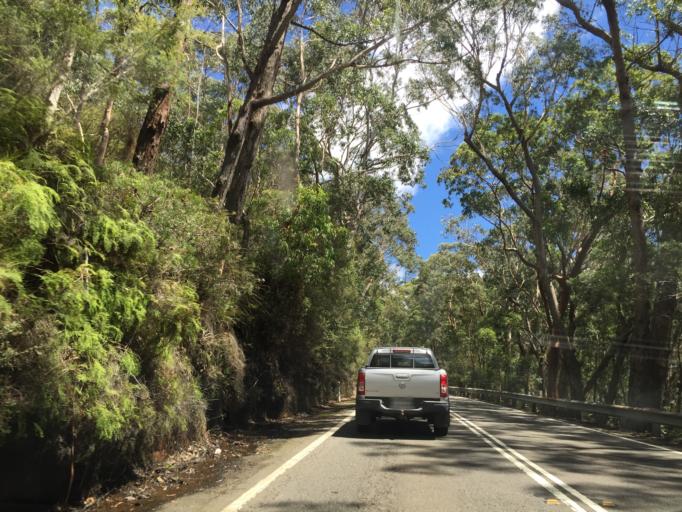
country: AU
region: New South Wales
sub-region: Blue Mountains Municipality
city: Blackheath
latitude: -33.5368
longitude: 150.4265
